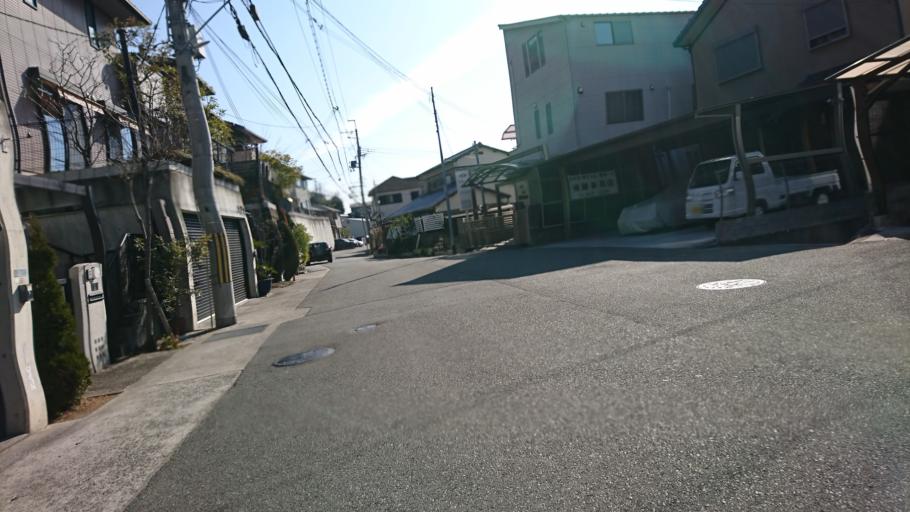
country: JP
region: Hyogo
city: Kakogawacho-honmachi
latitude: 34.7770
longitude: 134.7943
